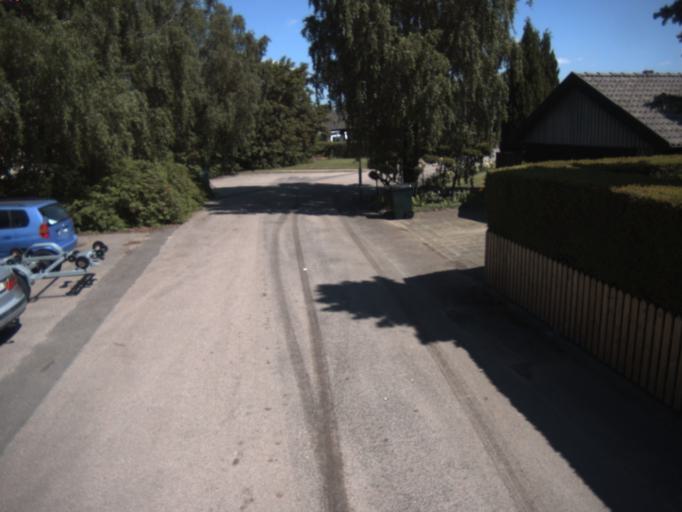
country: SE
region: Skane
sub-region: Helsingborg
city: Odakra
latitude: 56.1244
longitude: 12.6960
